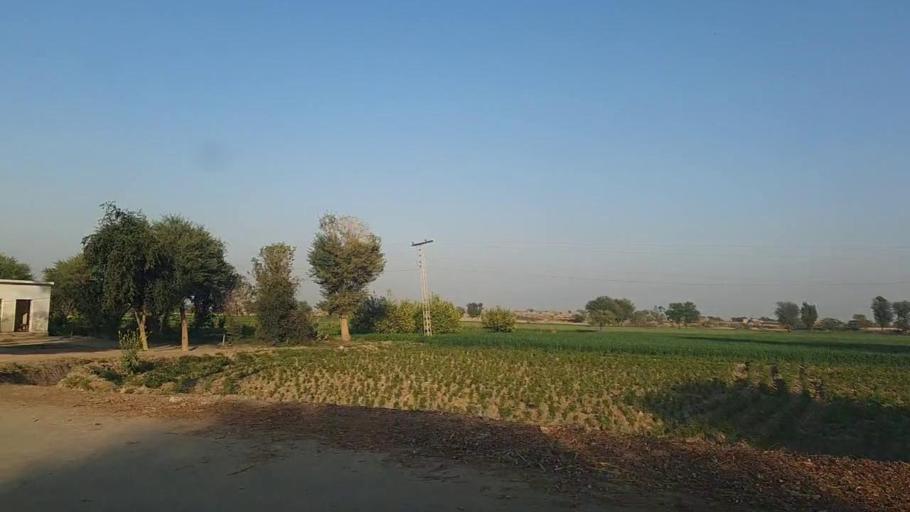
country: PK
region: Sindh
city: Jam Sahib
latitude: 26.3488
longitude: 68.6762
